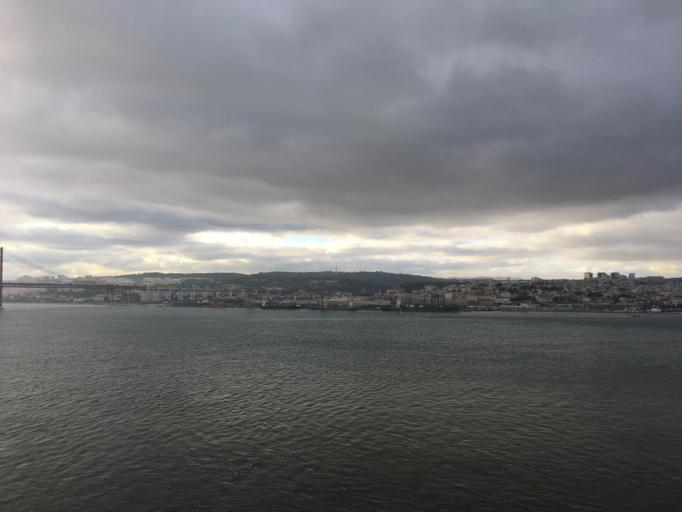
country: PT
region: Setubal
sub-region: Almada
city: Almada
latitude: 38.6846
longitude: -9.1569
